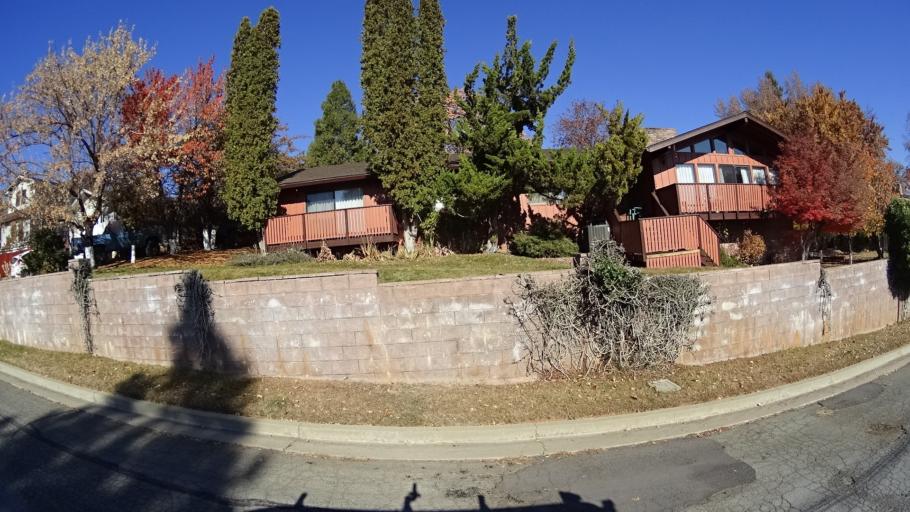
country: US
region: California
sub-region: Siskiyou County
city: Yreka
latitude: 41.7388
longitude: -122.6594
